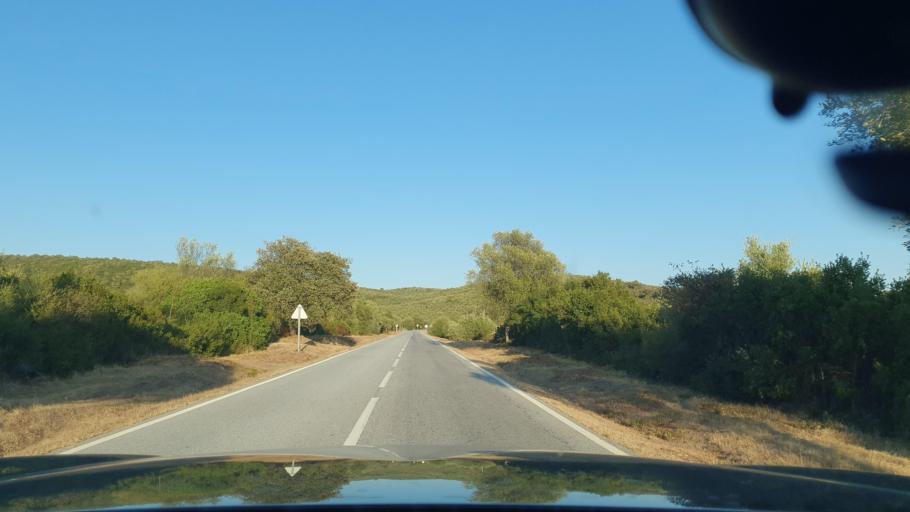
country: PT
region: Evora
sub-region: Estremoz
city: Estremoz
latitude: 38.9148
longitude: -7.6666
